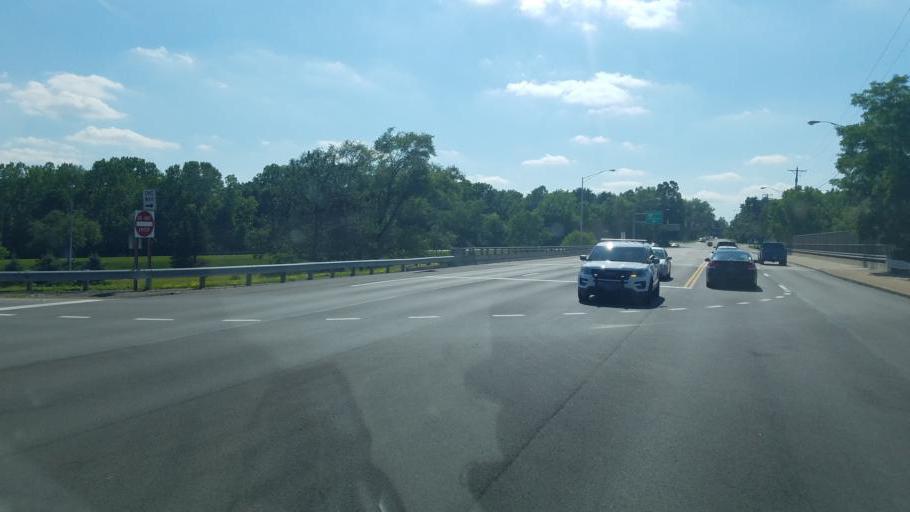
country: US
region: Ohio
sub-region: Franklin County
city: Worthington
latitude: 40.0894
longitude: -83.0349
